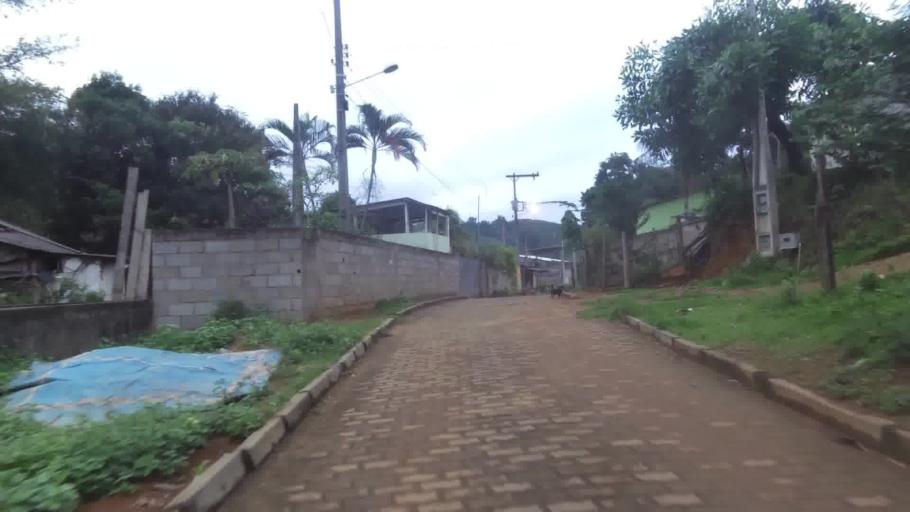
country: BR
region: Espirito Santo
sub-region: Iconha
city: Iconha
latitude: -20.7855
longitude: -40.8193
